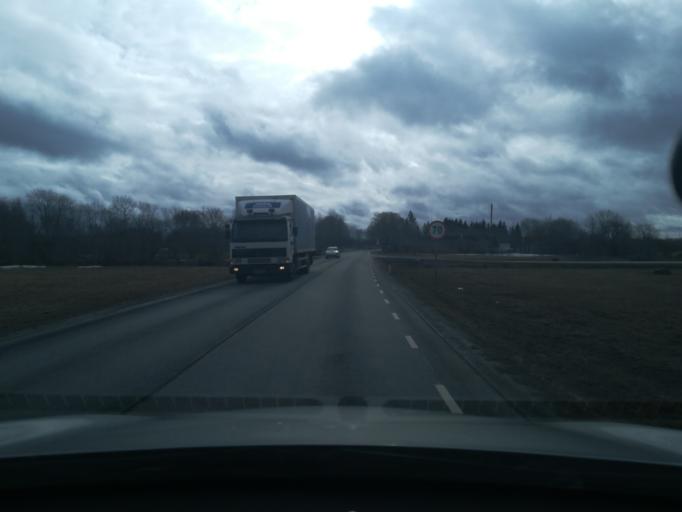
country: EE
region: Harju
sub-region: Harku vald
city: Tabasalu
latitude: 59.3927
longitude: 24.5560
